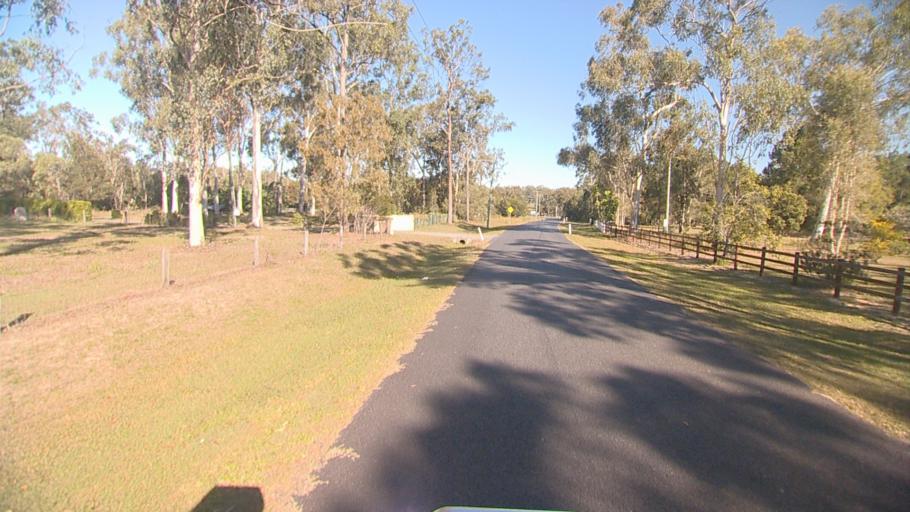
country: AU
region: Queensland
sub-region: Logan
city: Chambers Flat
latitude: -27.7319
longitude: 153.0720
